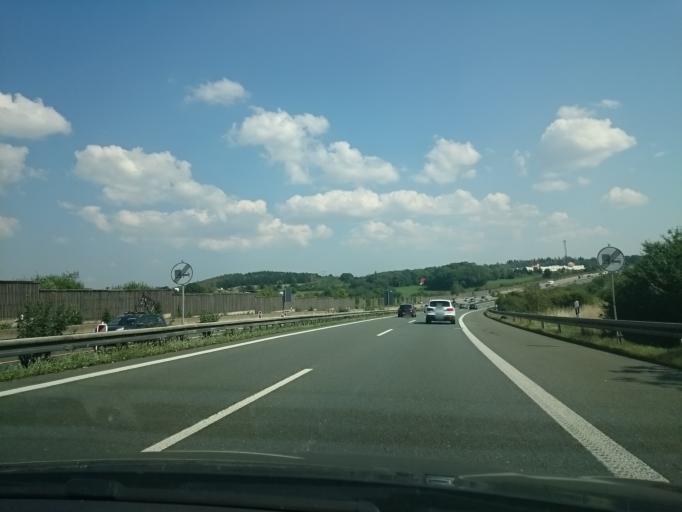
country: DE
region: Saxony
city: Weischlitz
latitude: 50.4331
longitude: 12.0797
